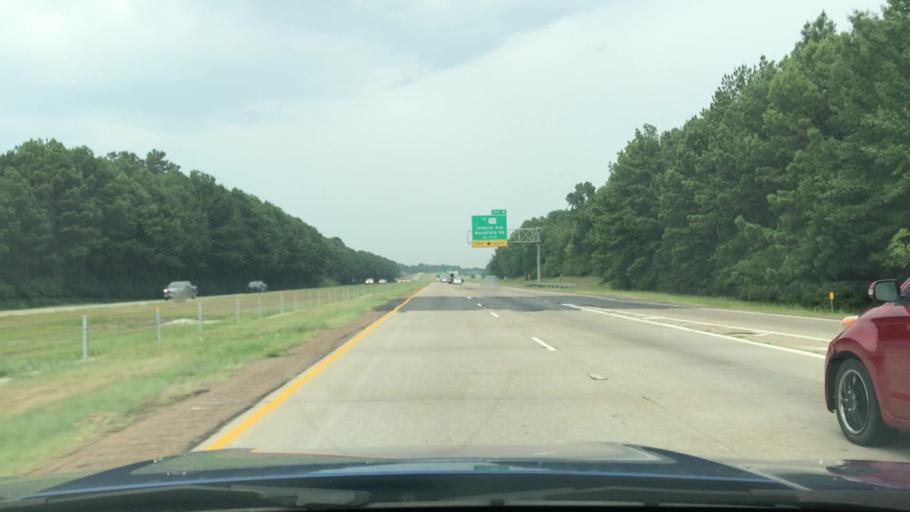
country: US
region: Louisiana
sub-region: Caddo Parish
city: Shreveport
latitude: 32.4172
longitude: -93.8114
